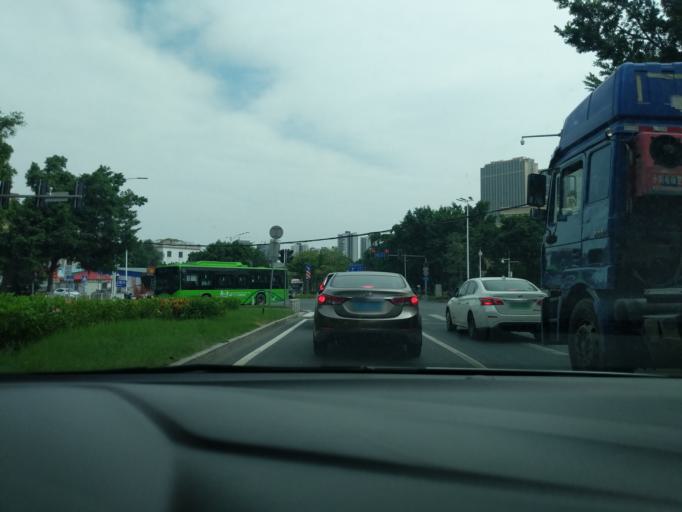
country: CN
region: Guangdong
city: Nansha
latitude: 22.7522
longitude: 113.5775
